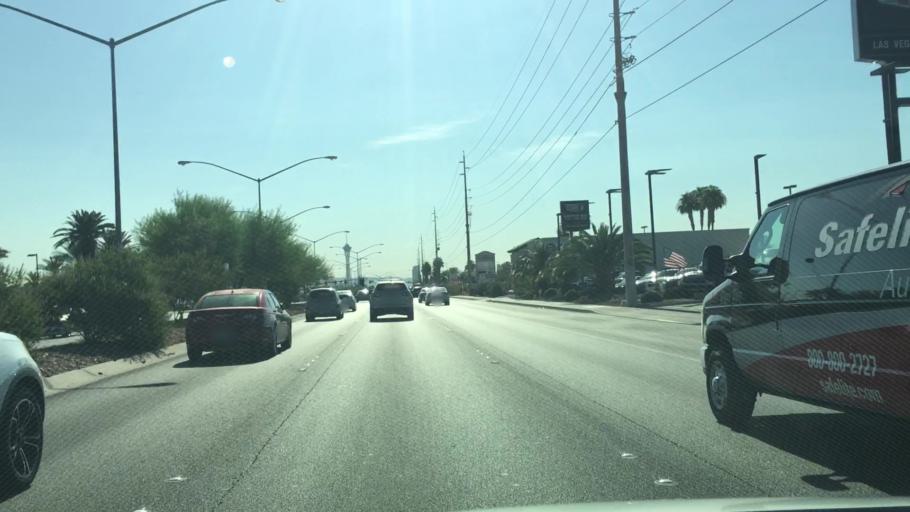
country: US
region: Nevada
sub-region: Clark County
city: Spring Valley
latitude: 36.1444
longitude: -115.2121
